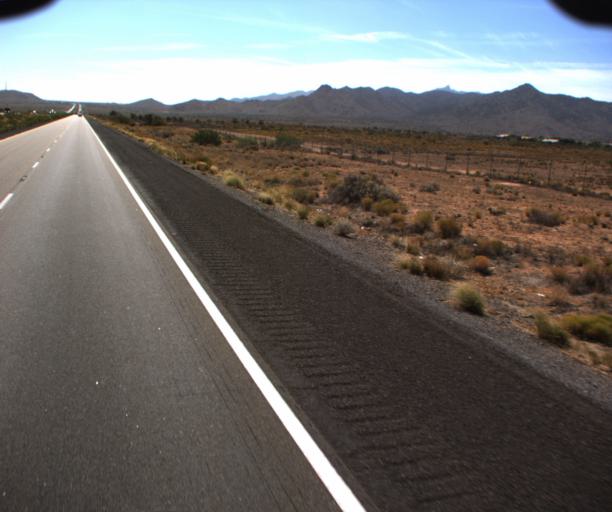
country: US
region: Arizona
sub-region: Mohave County
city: New Kingman-Butler
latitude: 35.2098
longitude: -113.9648
